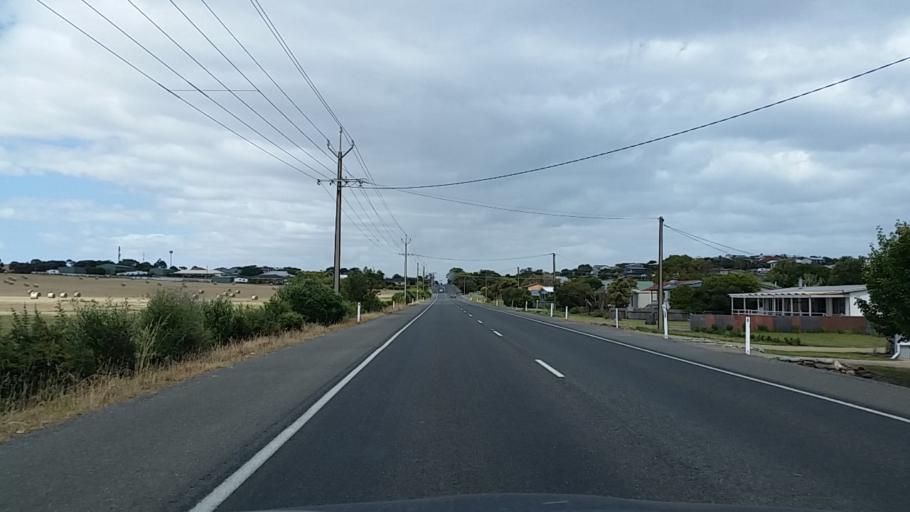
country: AU
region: South Australia
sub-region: Alexandrina
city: Port Elliot
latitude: -35.5324
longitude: 138.6664
